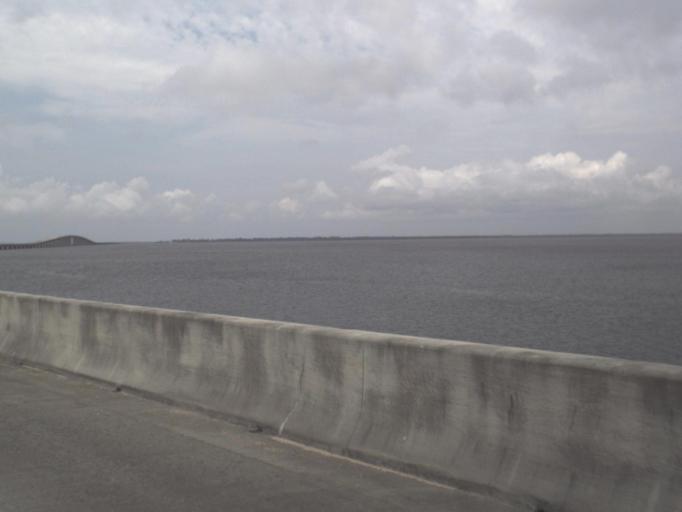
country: US
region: Florida
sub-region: Santa Rosa County
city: Tiger Point
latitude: 30.3989
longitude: -87.0762
